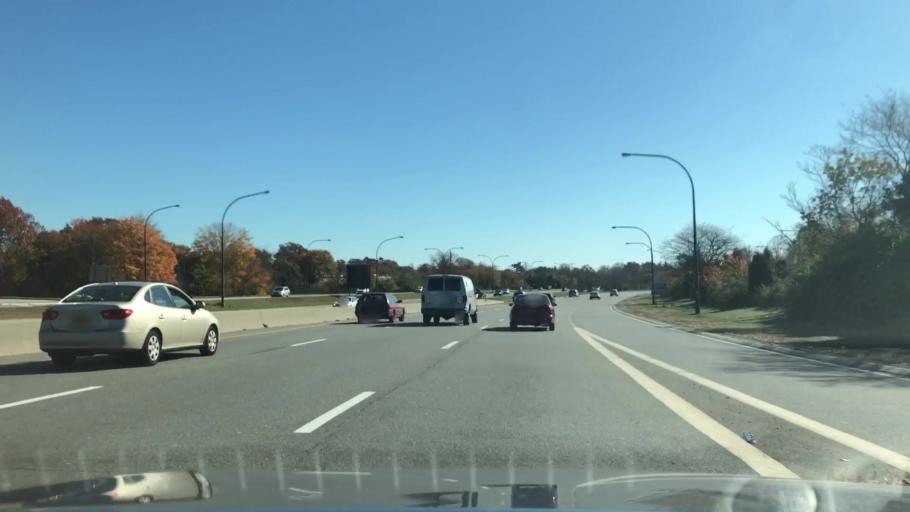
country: US
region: New York
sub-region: Nassau County
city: East Garden City
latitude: 40.7344
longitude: -73.5852
